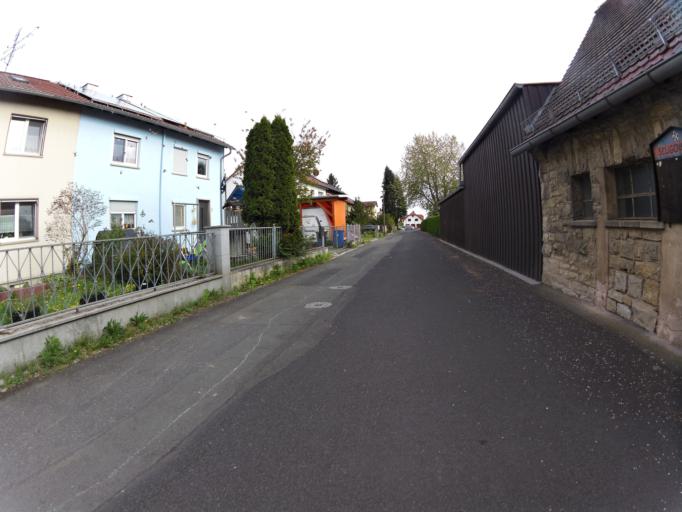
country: DE
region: Bavaria
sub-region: Regierungsbezirk Unterfranken
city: Oberpleichfeld
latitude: 49.8546
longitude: 10.1014
